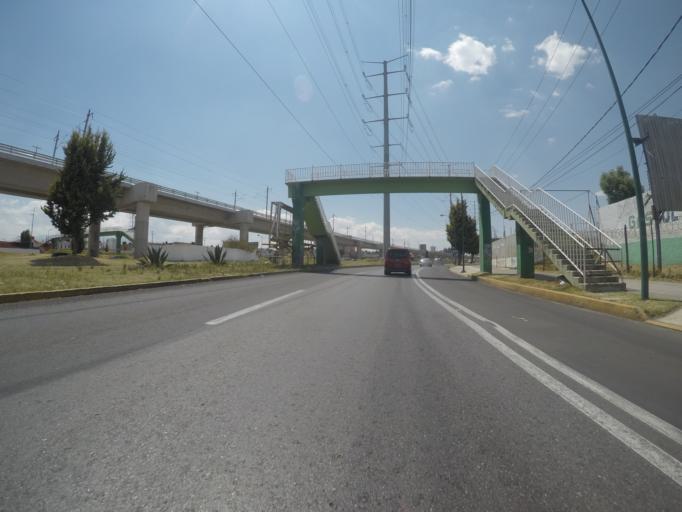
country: MX
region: Mexico
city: San Buenaventura
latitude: 19.2679
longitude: -99.6542
